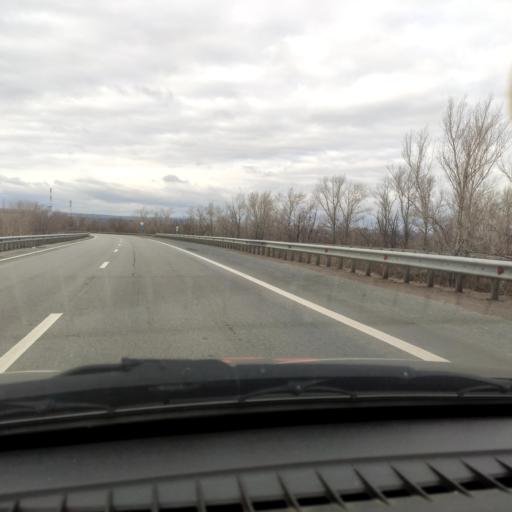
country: RU
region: Samara
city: Novosemeykino
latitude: 53.4171
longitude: 50.3376
